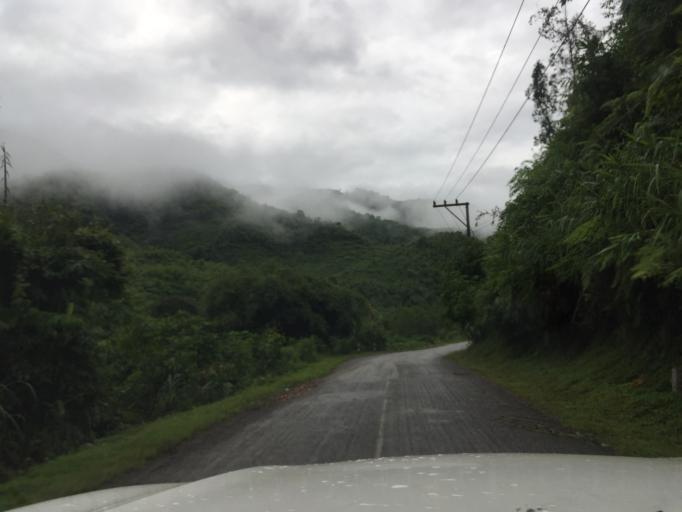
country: LA
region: Oudomxai
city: Muang La
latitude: 20.9327
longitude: 102.2064
